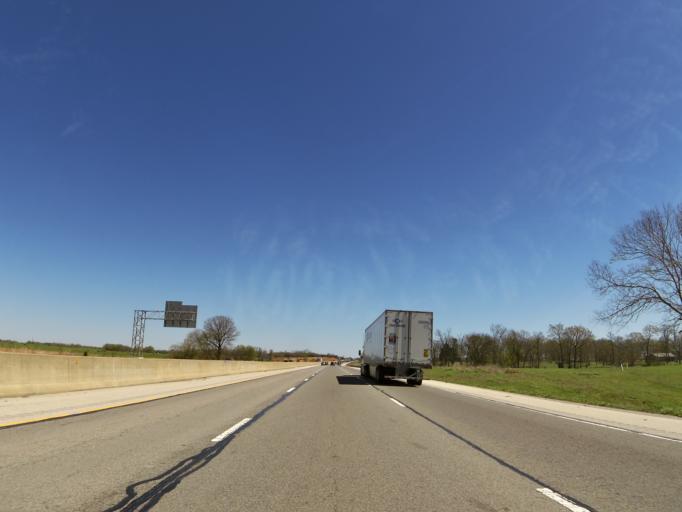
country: US
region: Kentucky
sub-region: Warren County
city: Bowling Green
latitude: 37.0109
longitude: -86.3410
